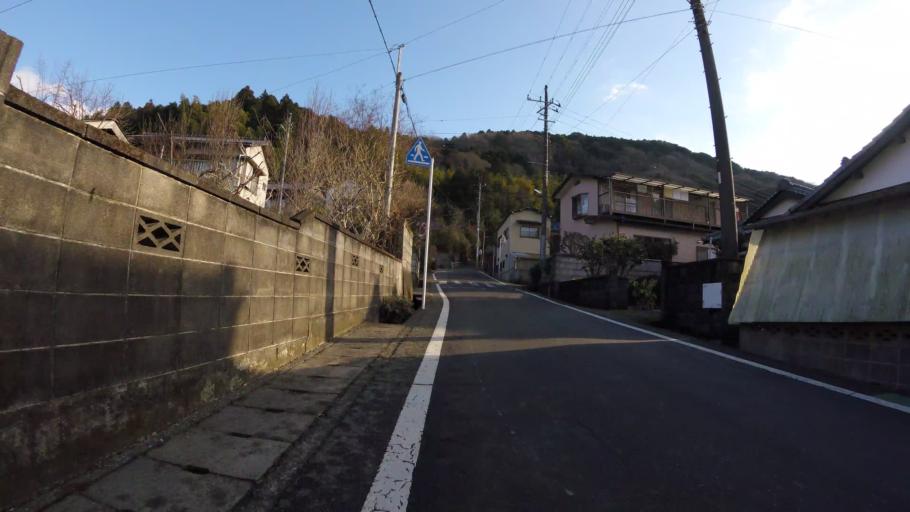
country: JP
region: Shizuoka
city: Atami
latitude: 35.1174
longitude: 139.0167
